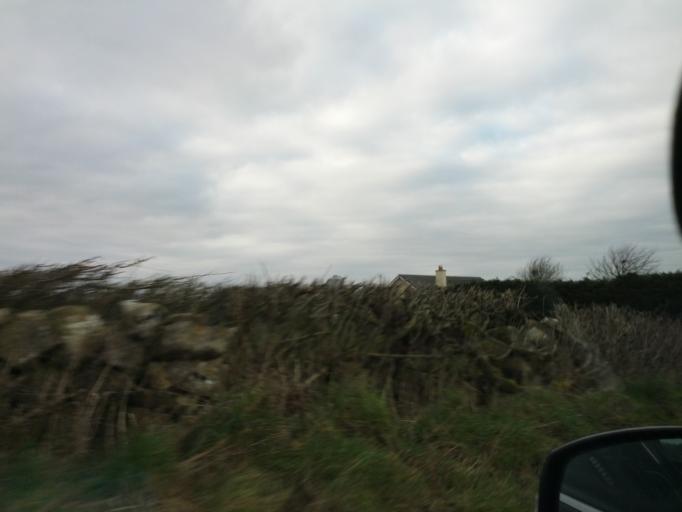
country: IE
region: Connaught
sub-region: County Galway
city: Gort
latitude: 53.1702
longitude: -8.8503
